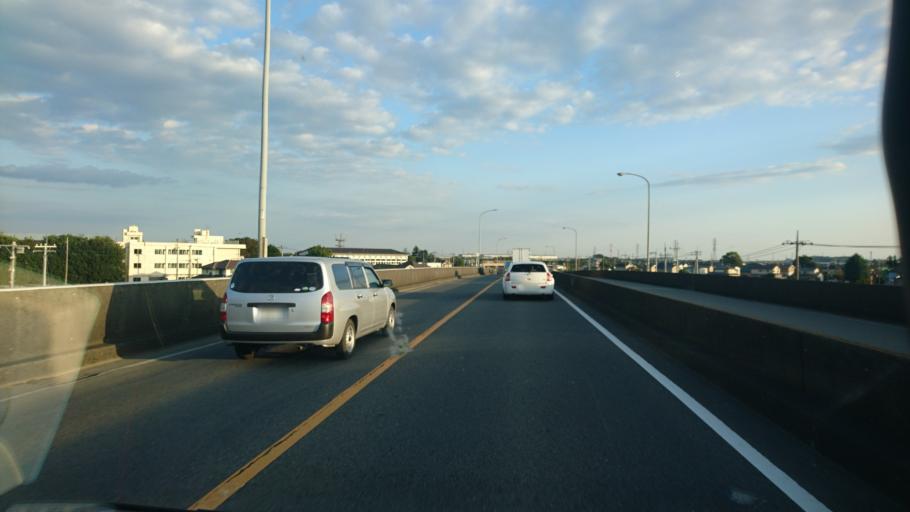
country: JP
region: Gunma
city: Ota
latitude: 36.3383
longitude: 139.3880
